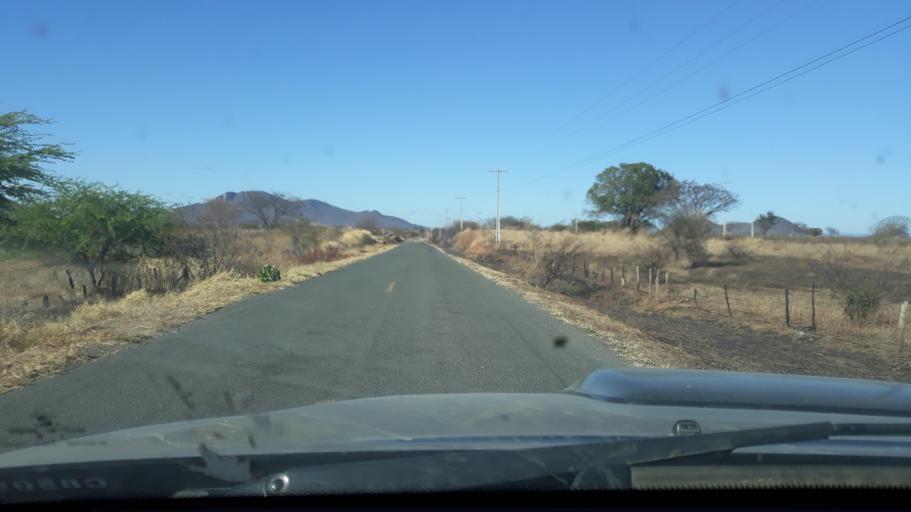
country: BR
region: Bahia
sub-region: Guanambi
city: Guanambi
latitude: -14.0008
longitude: -42.8581
